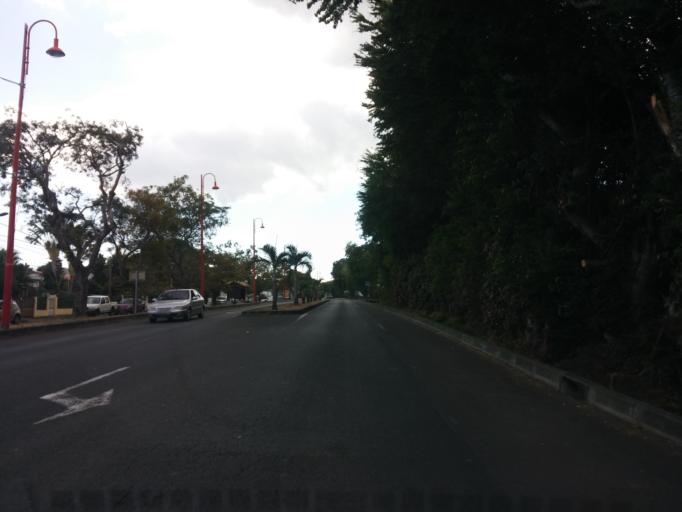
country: RE
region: Reunion
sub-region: Reunion
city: La Possession
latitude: -20.9372
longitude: 55.3327
